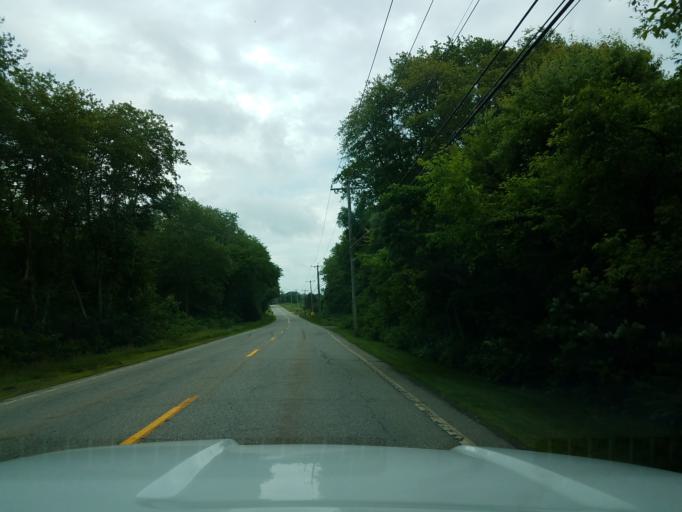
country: US
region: Connecticut
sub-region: New London County
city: Preston City
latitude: 41.5305
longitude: -71.9945
